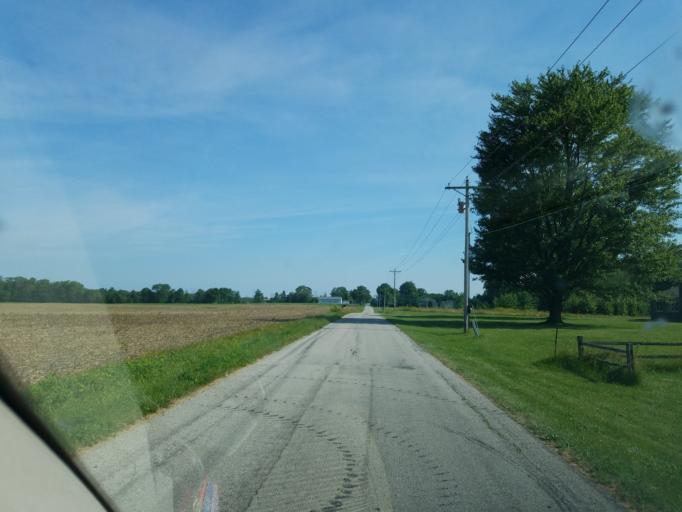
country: US
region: Ohio
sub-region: Morrow County
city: Cardington
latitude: 40.6197
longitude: -82.9528
